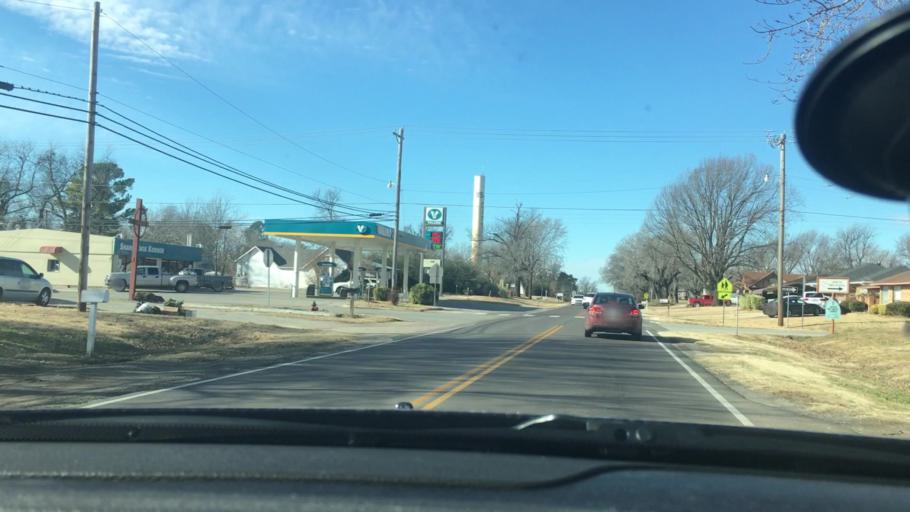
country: US
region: Oklahoma
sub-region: Cleveland County
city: Lexington
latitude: 35.0149
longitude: -97.3272
